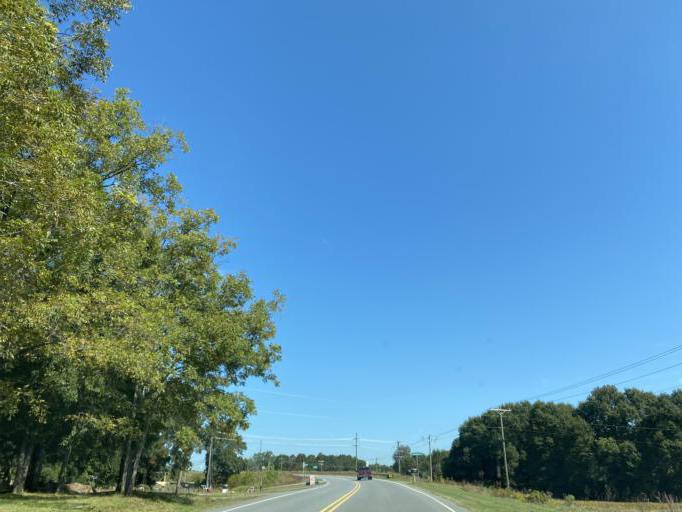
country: US
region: North Carolina
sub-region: Cleveland County
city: Boiling Springs
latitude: 35.2923
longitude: -81.6702
